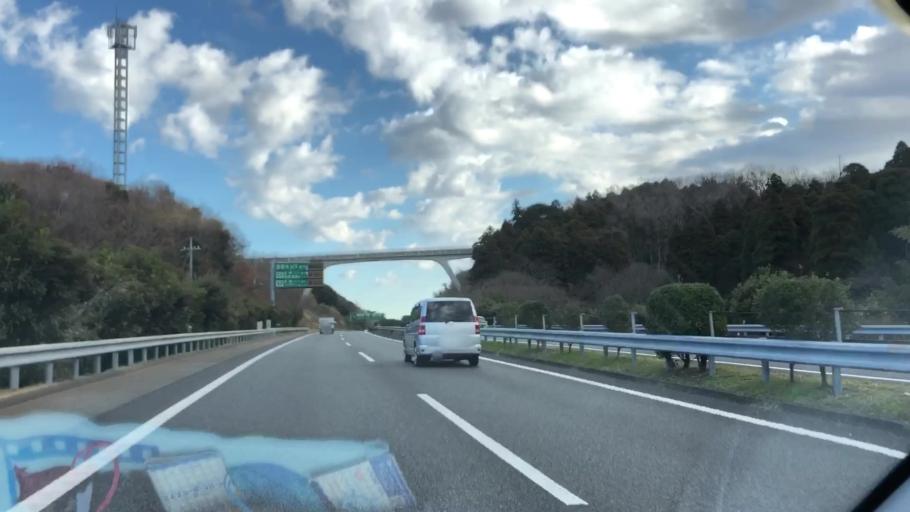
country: JP
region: Chiba
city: Kisarazu
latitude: 35.3664
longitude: 139.9627
